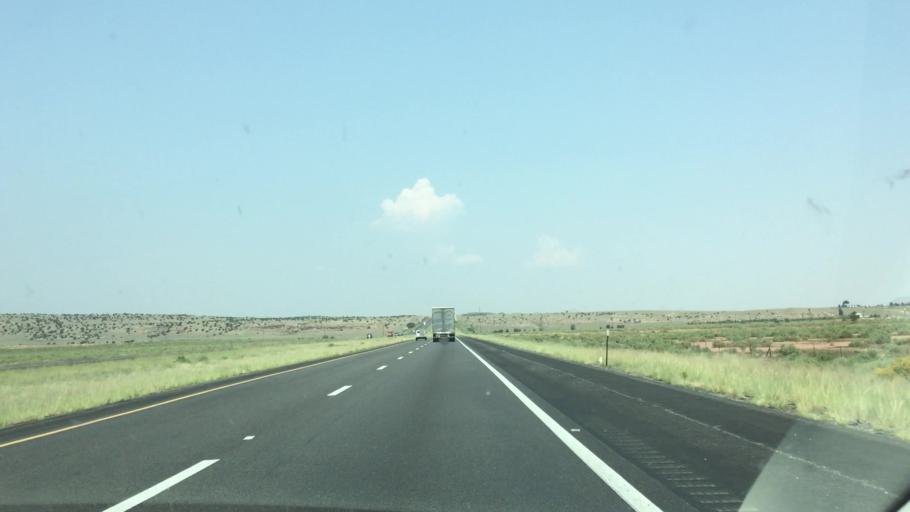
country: US
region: New Mexico
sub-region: Cibola County
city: Milan
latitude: 35.1981
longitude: -107.9142
